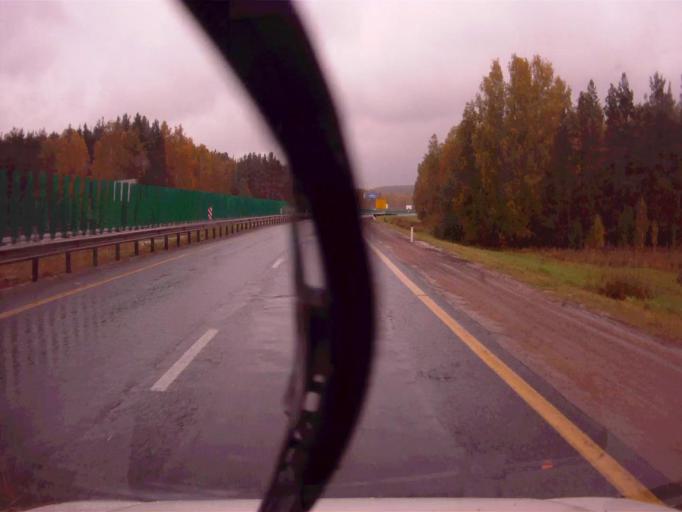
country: RU
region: Chelyabinsk
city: Dolgoderevenskoye
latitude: 55.3384
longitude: 61.3078
